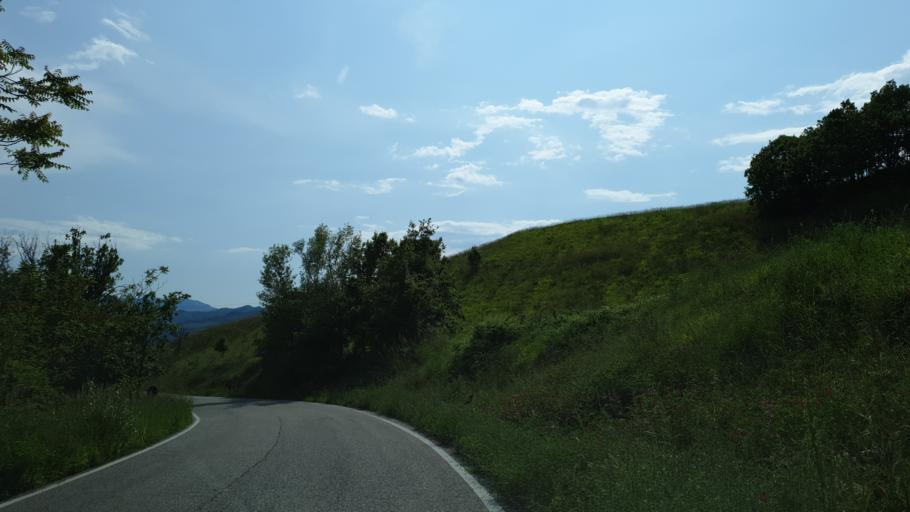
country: IT
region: Emilia-Romagna
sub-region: Forli-Cesena
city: Sarsina
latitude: 43.9100
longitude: 12.1892
